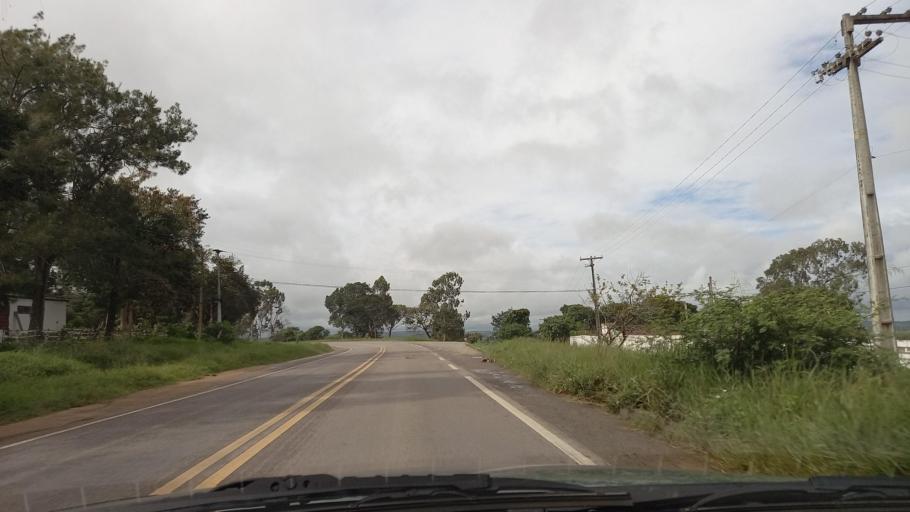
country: BR
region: Pernambuco
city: Garanhuns
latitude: -8.9100
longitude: -36.4958
